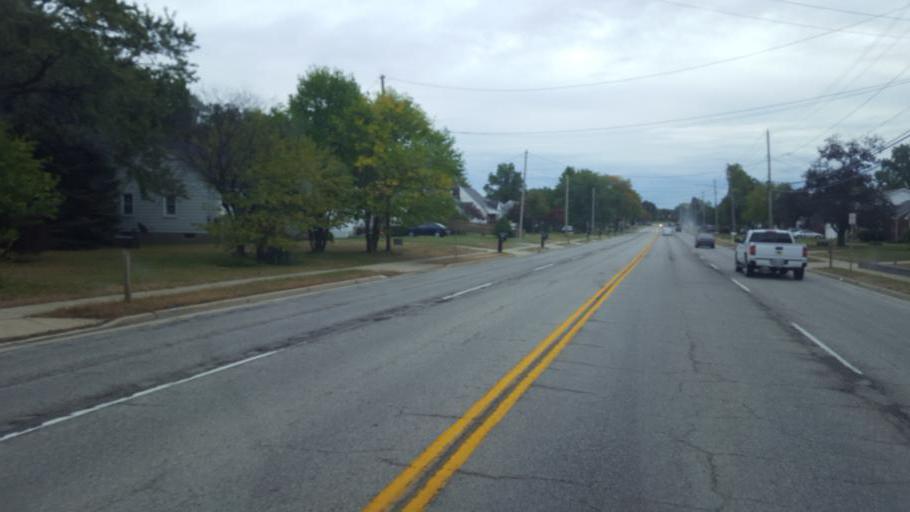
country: US
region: Ohio
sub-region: Lorain County
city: Lorain
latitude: 41.4217
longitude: -82.1628
